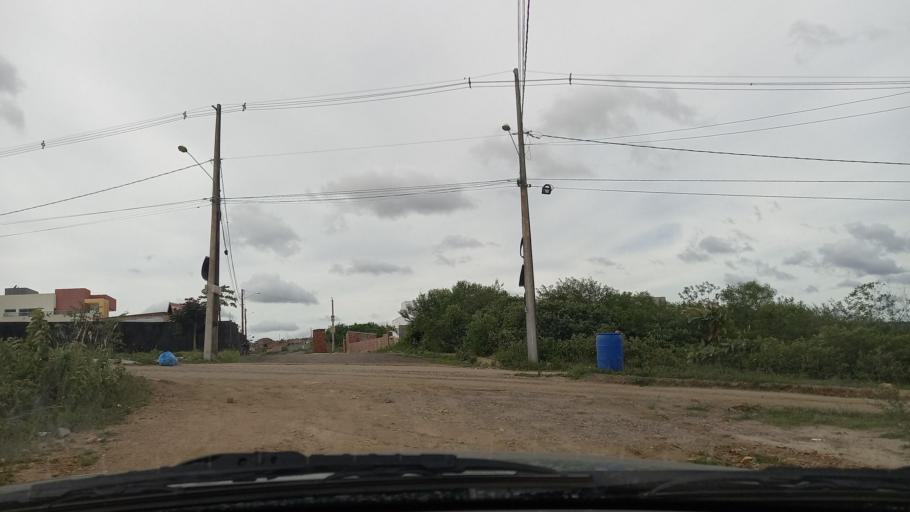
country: BR
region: Pernambuco
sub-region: Gravata
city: Gravata
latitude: -8.2216
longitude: -35.5759
